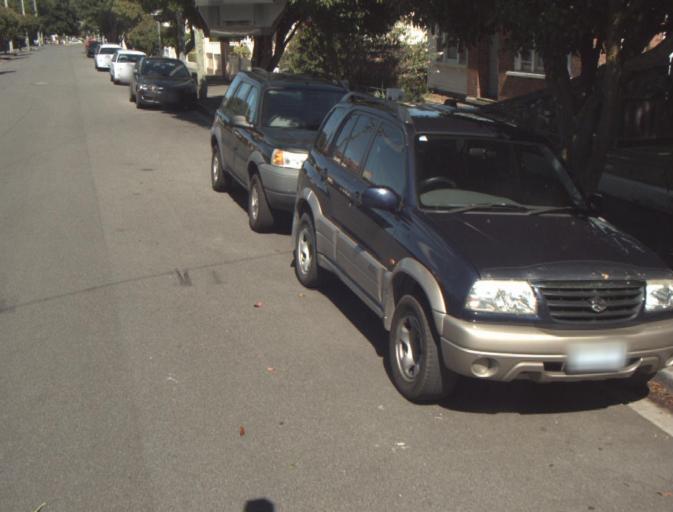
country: AU
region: Tasmania
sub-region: Launceston
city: Launceston
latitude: -41.4178
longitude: 147.1377
